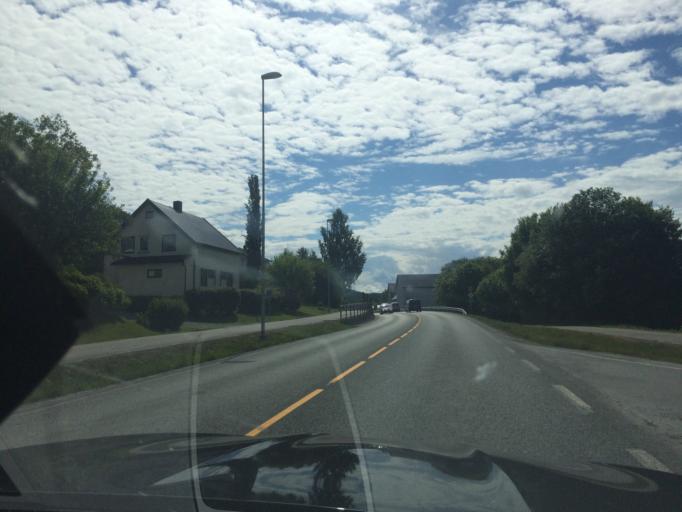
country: NO
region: Nord-Trondelag
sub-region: Steinkjer
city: Steinkjer
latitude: 63.9216
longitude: 11.4323
